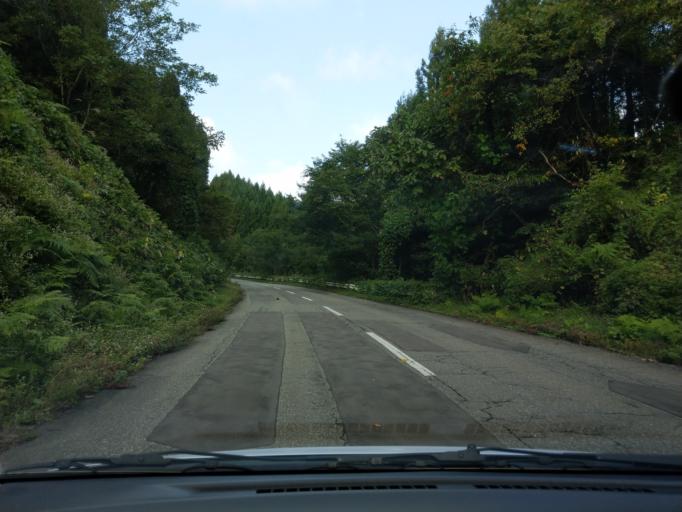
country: JP
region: Akita
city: Omagari
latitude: 39.4700
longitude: 140.3184
